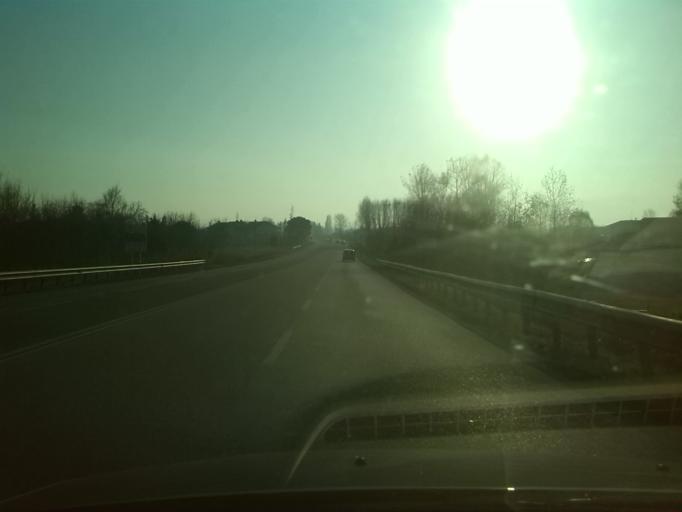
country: IT
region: Friuli Venezia Giulia
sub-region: Provincia di Udine
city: Latisana
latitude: 45.7872
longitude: 13.0232
